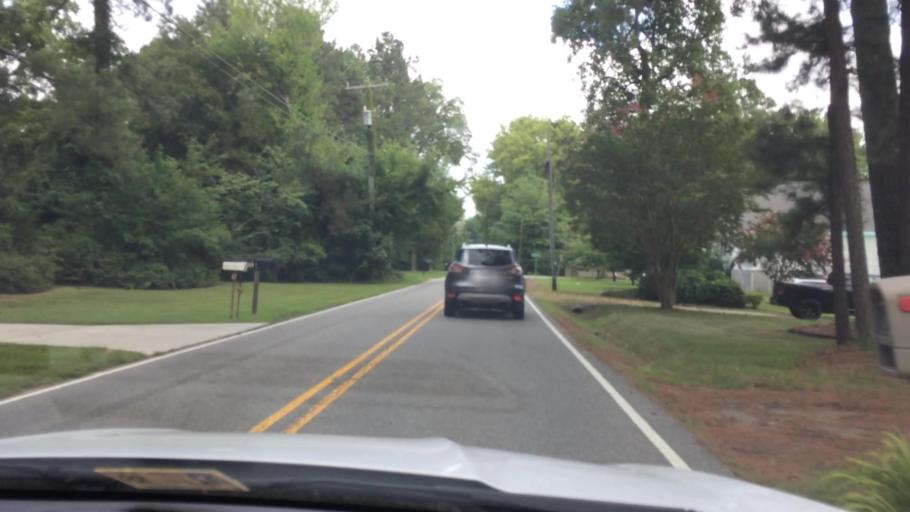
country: US
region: Virginia
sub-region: City of Poquoson
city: Poquoson
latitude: 37.1452
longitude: -76.4473
